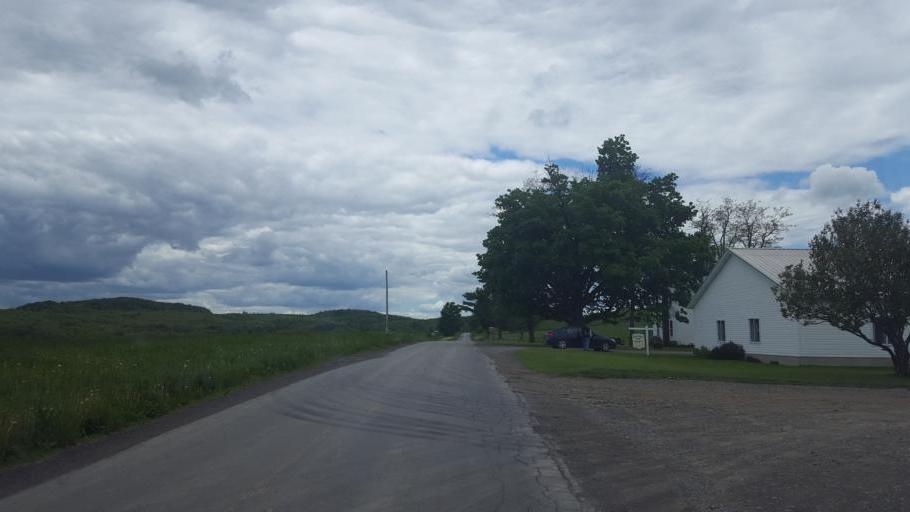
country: US
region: New York
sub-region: Otsego County
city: Richfield Springs
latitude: 42.8692
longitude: -75.0635
